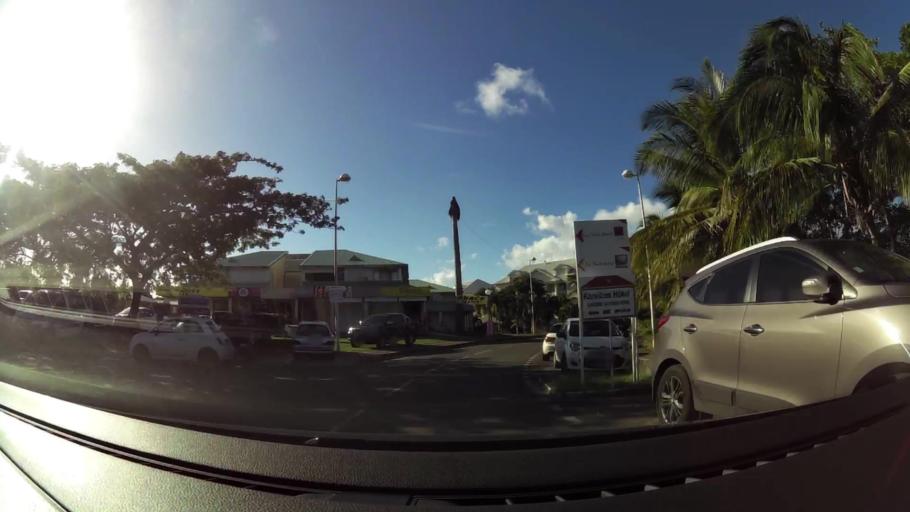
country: GP
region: Guadeloupe
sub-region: Guadeloupe
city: Le Gosier
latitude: 16.2084
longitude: -61.5056
